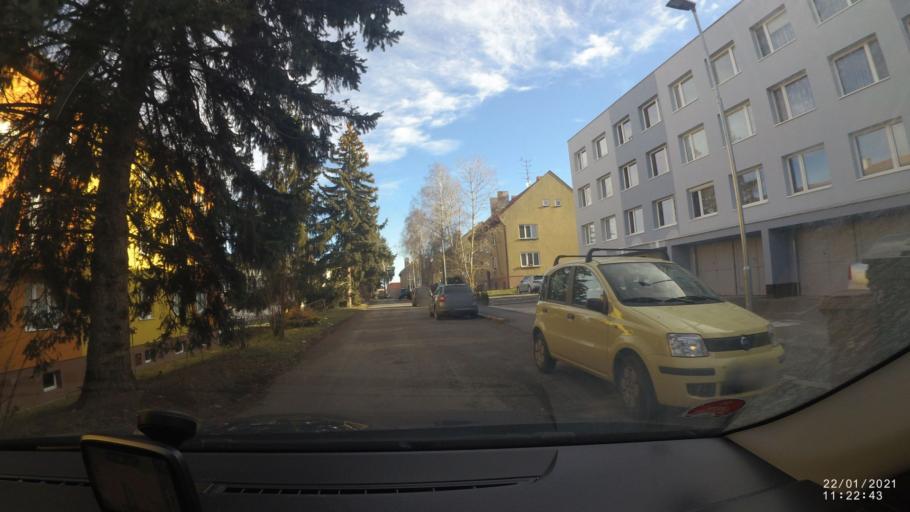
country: CZ
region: Central Bohemia
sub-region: Okres Beroun
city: Horovice
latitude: 49.8321
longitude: 13.8986
